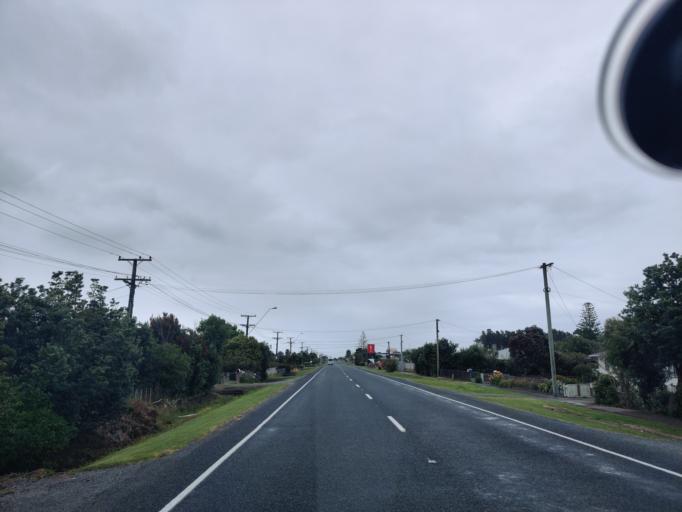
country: NZ
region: Northland
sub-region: Kaipara District
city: Dargaville
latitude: -36.1299
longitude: 174.0184
